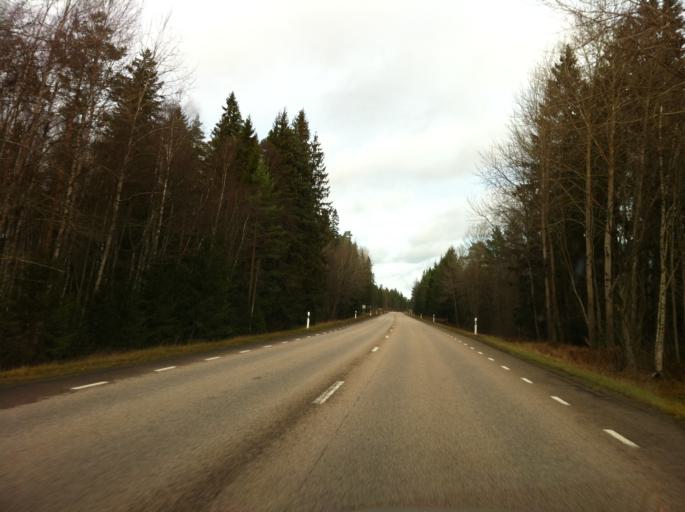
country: SE
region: Kronoberg
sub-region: Uppvidinge Kommun
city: Lenhovda
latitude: 57.1149
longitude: 15.2168
